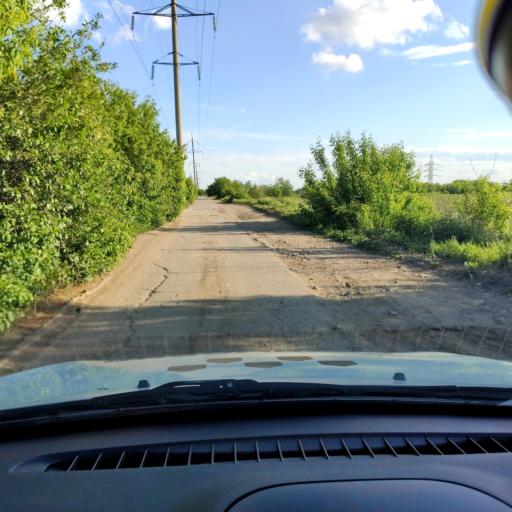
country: RU
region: Samara
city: Tol'yatti
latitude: 53.5892
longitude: 49.4358
